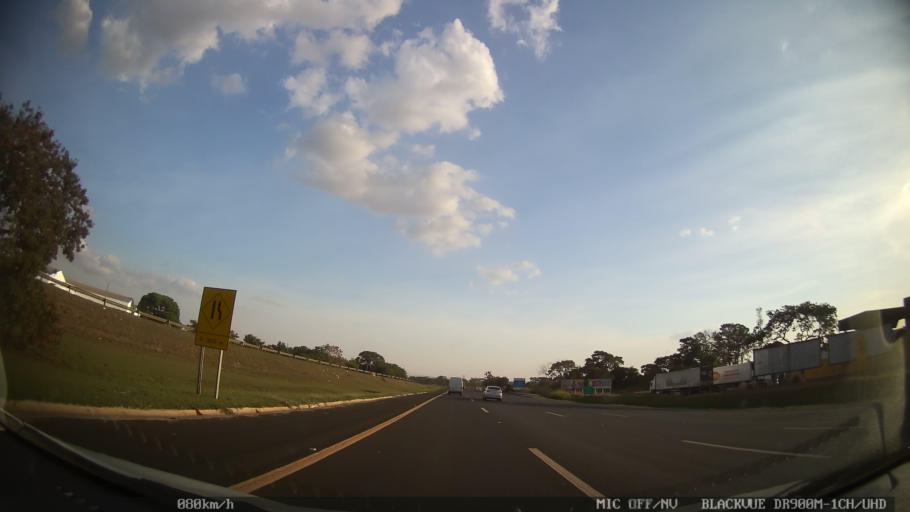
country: BR
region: Sao Paulo
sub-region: Ribeirao Preto
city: Ribeirao Preto
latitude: -21.1149
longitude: -47.7826
